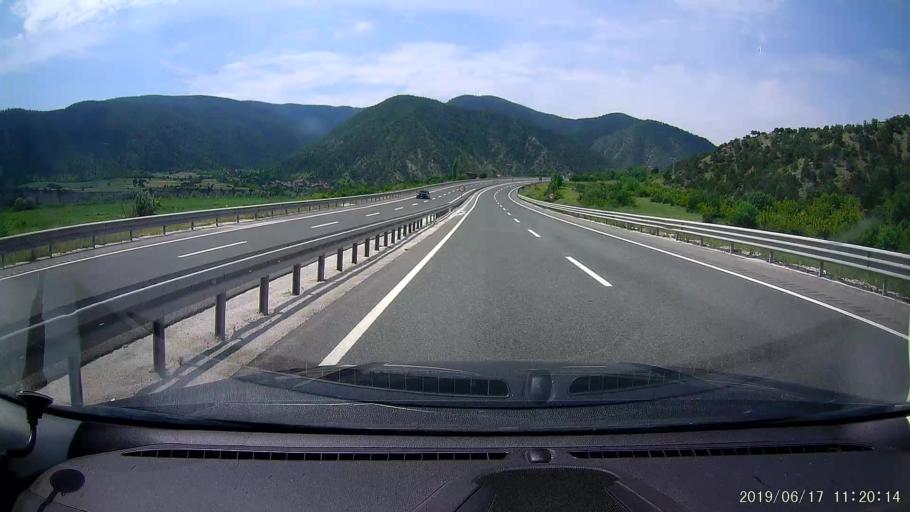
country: TR
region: Cankiri
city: Yaprakli
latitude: 40.9155
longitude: 33.8118
